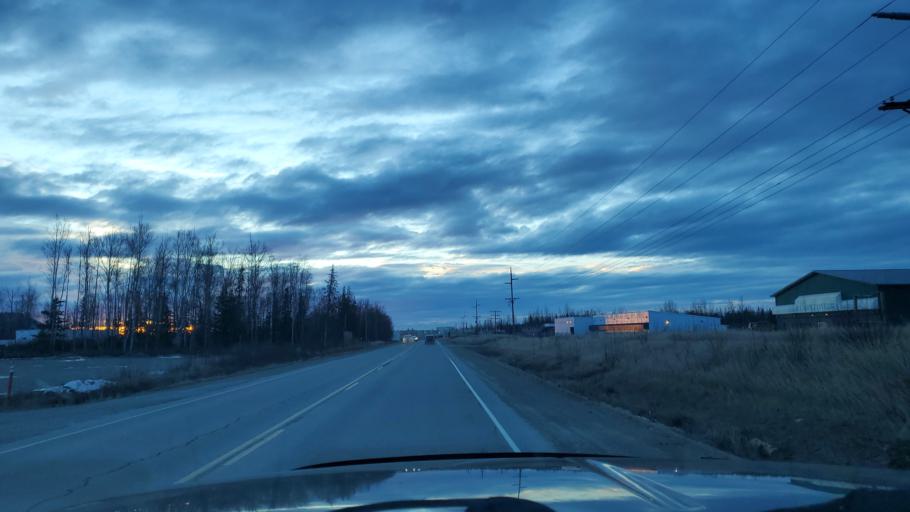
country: US
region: Alaska
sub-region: Matanuska-Susitna Borough
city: Wasilla
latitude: 61.5918
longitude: -149.3960
